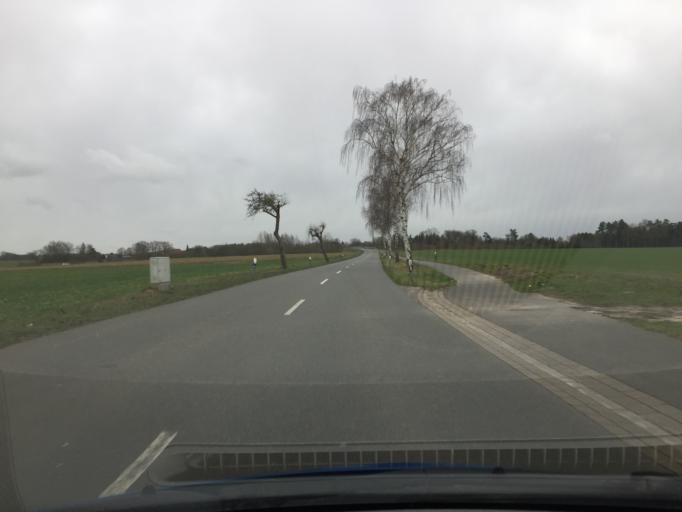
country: DE
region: Lower Saxony
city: Uelzen
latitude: 52.9472
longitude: 10.5749
